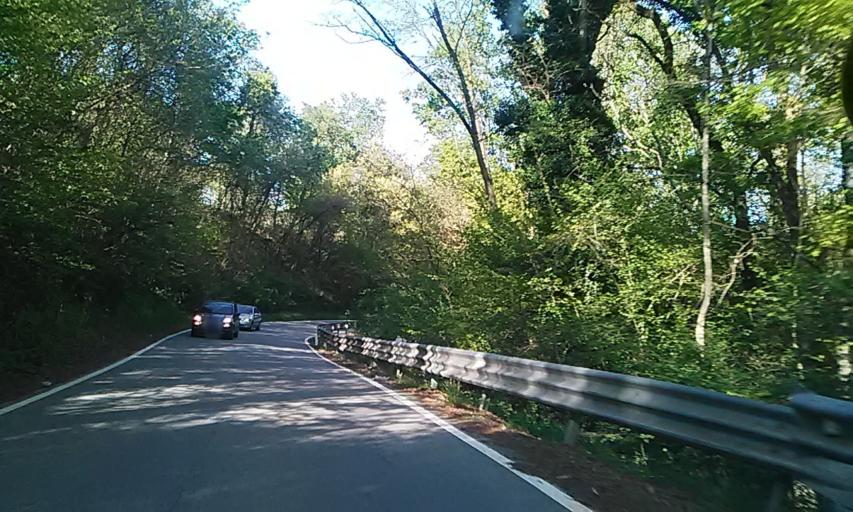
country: IT
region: Piedmont
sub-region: Provincia di Novara
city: Ghemme
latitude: 45.6136
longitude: 8.4461
